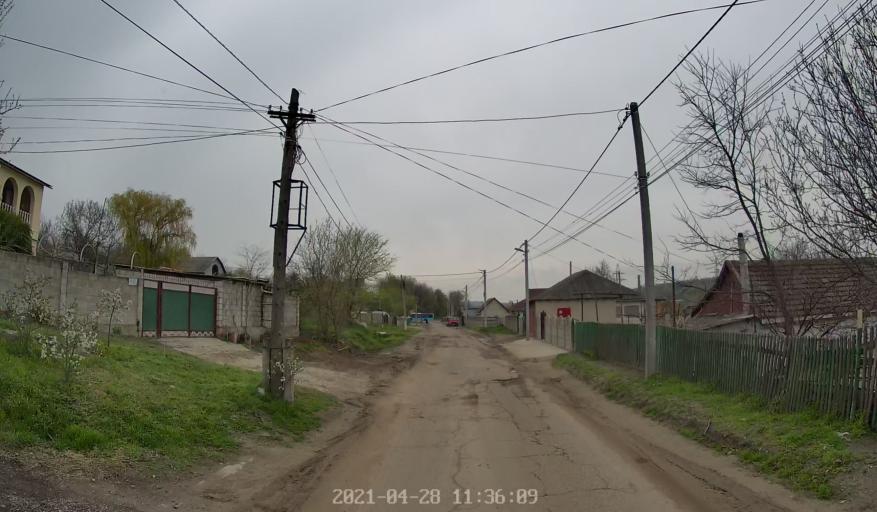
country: MD
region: Chisinau
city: Singera
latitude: 46.9458
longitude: 28.9484
